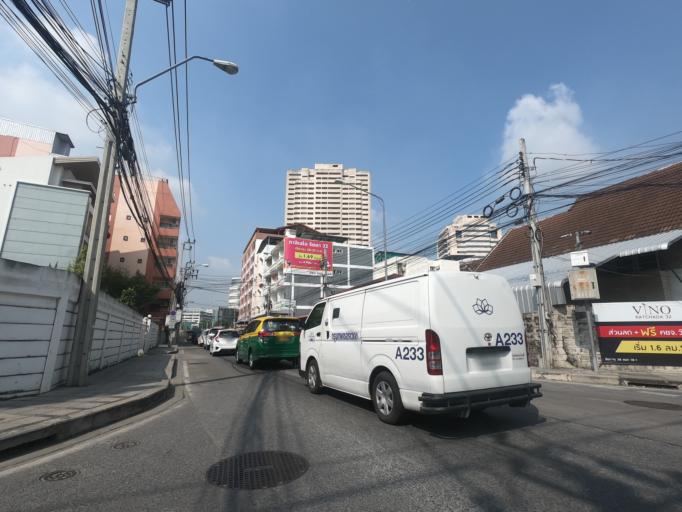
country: TH
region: Bangkok
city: Chatuchak
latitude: 13.8165
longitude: 100.5781
